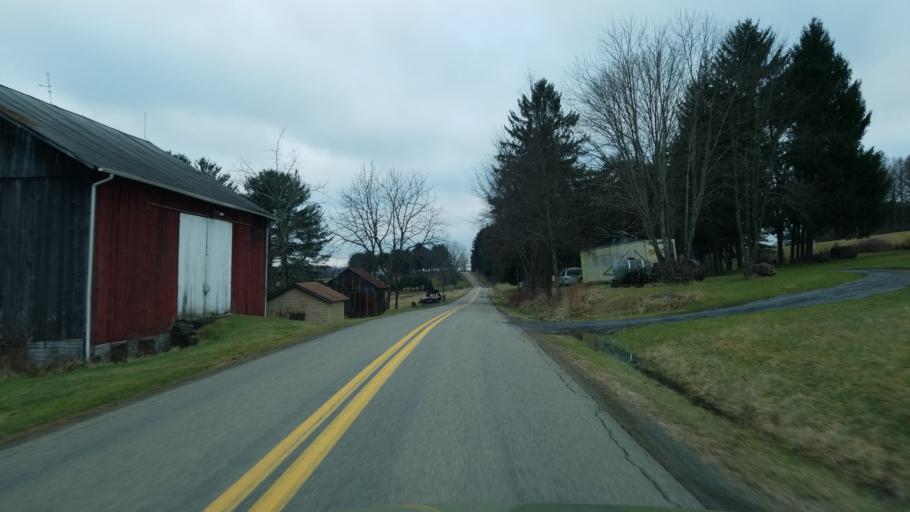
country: US
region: Pennsylvania
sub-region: Jefferson County
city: Falls Creek
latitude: 41.1642
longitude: -78.8121
